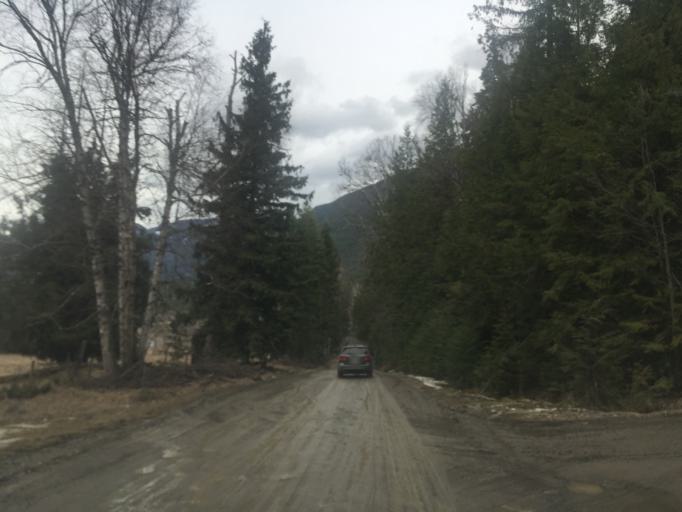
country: CA
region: British Columbia
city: Chase
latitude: 51.3758
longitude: -120.1340
